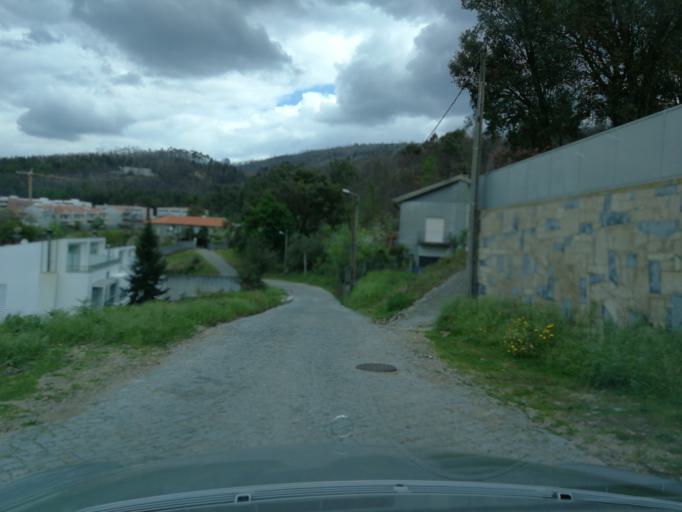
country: PT
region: Braga
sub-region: Braga
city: Braga
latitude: 41.5249
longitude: -8.3962
